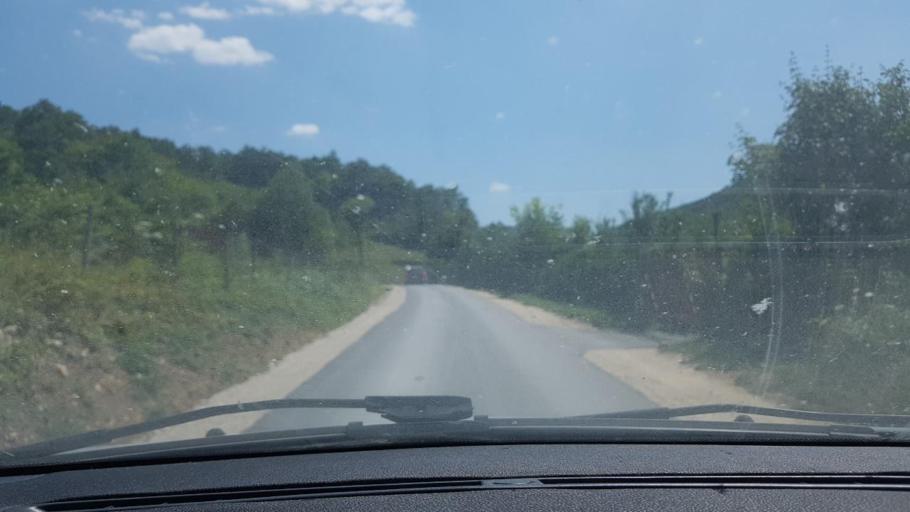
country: BA
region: Federation of Bosnia and Herzegovina
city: Orasac
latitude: 44.6448
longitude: 16.0367
